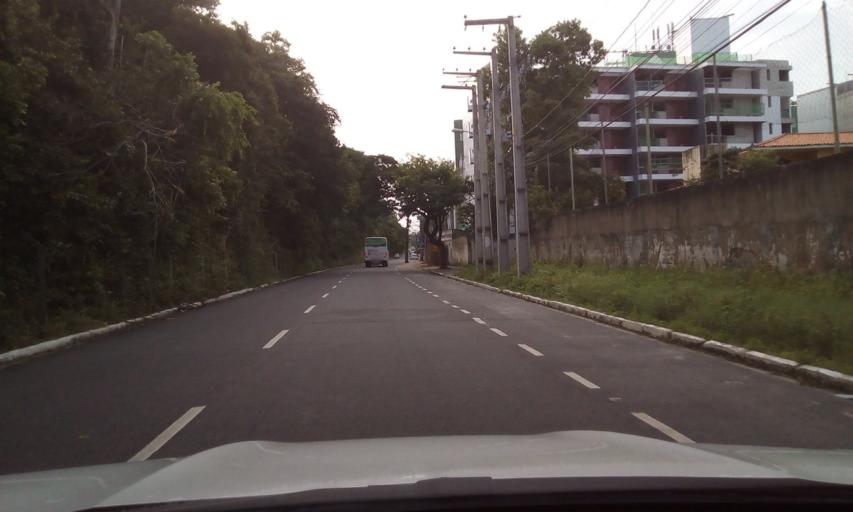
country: BR
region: Paraiba
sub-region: Joao Pessoa
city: Joao Pessoa
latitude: -7.1364
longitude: -34.8210
